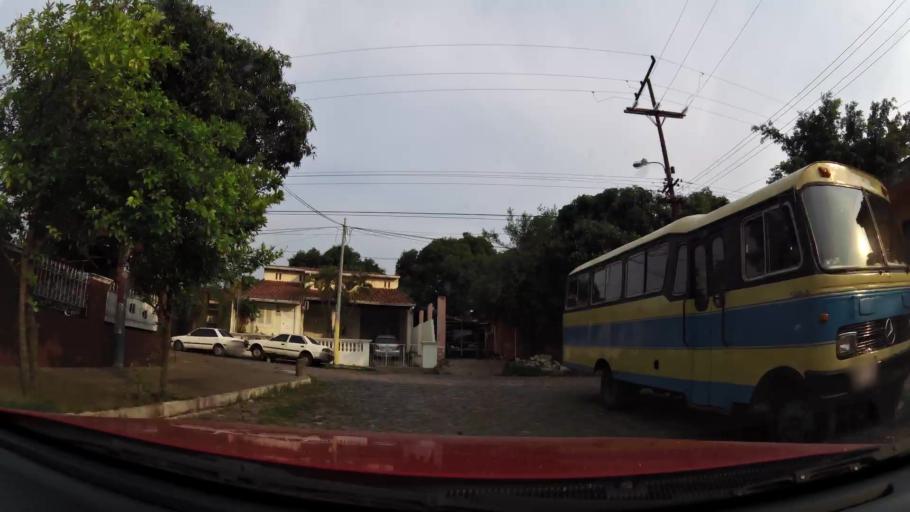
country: PY
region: Central
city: Lambare
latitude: -25.3280
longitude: -57.5788
